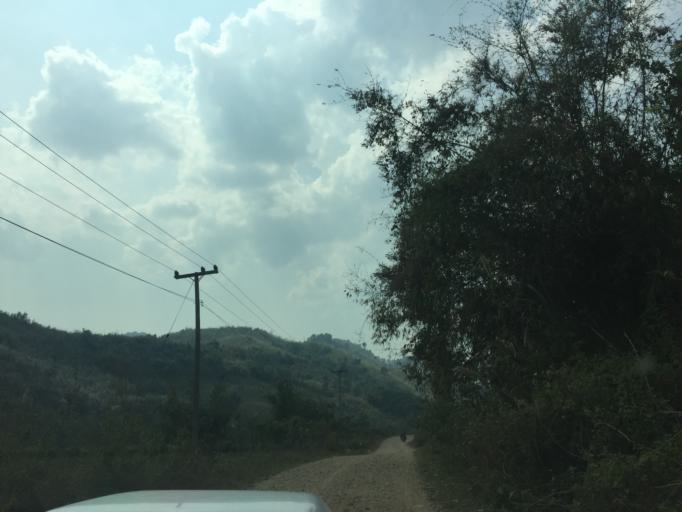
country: TH
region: Nan
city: Song Khwae
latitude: 19.7322
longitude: 100.7300
